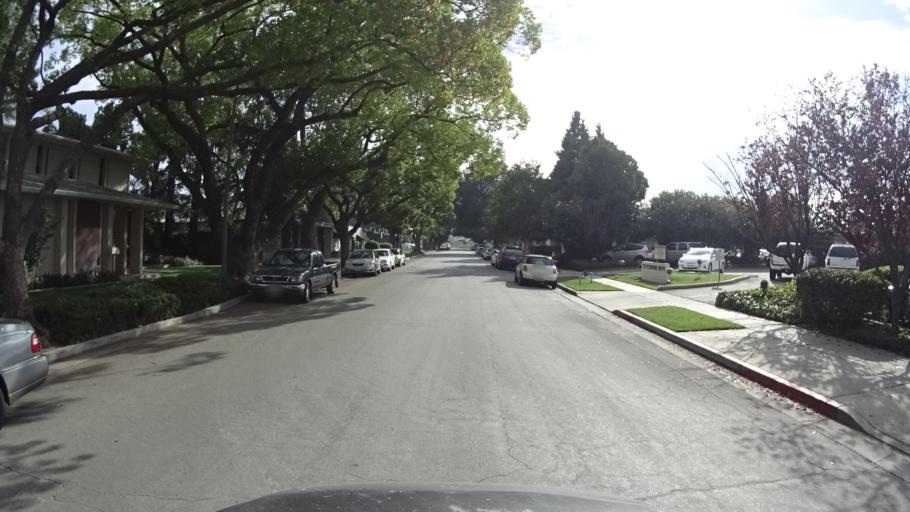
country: US
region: California
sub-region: Santa Clara County
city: Burbank
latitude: 37.3262
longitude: -121.9399
